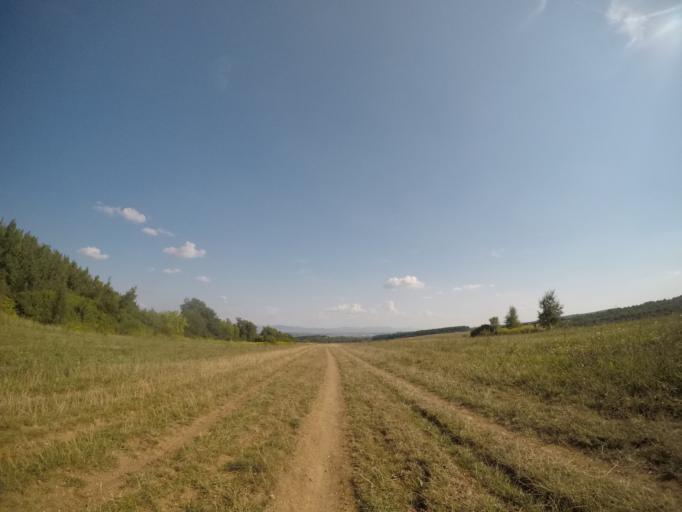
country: SK
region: Kosicky
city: Kosice
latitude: 48.7346
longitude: 21.2122
